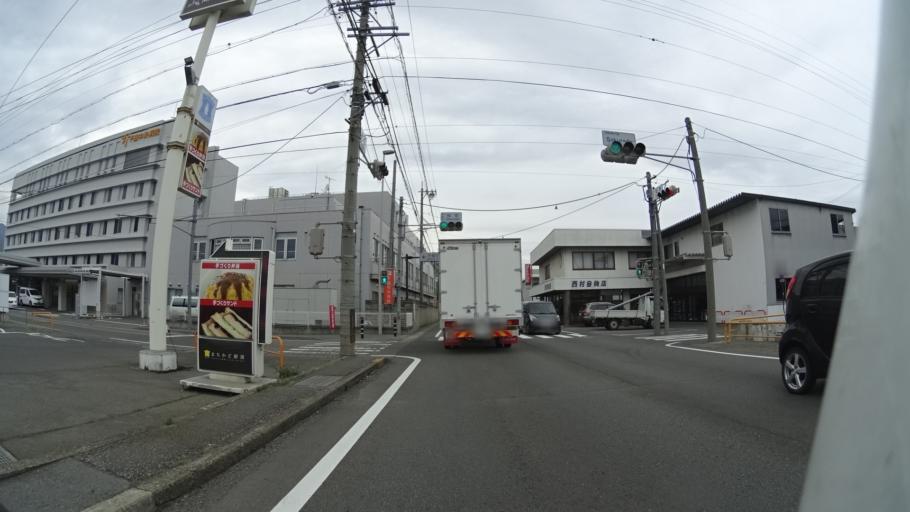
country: JP
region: Nagano
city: Nagano-shi
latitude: 36.5298
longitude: 138.1234
